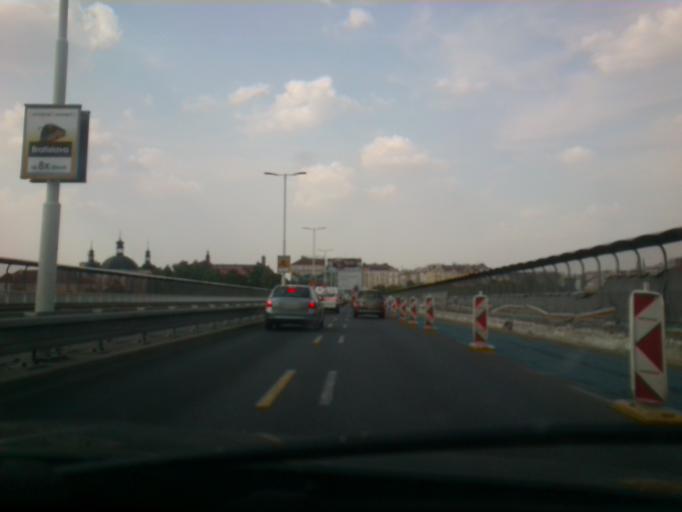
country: CZ
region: Praha
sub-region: Praha 2
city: Vysehrad
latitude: 50.0652
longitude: 14.4304
